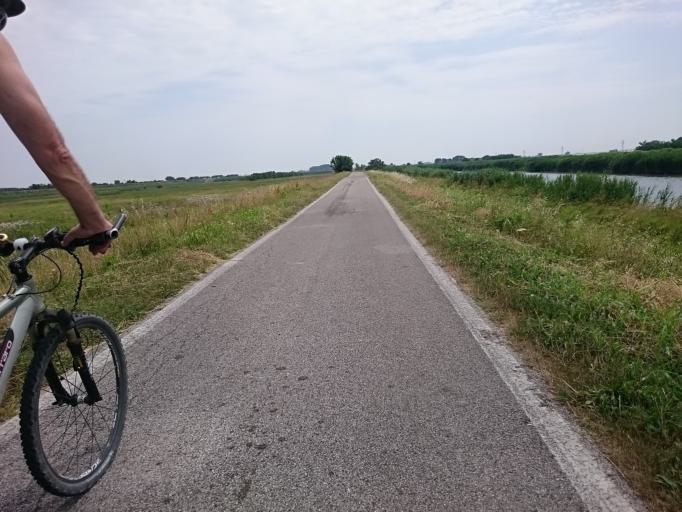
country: IT
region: Veneto
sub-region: Provincia di Venezia
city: Valli
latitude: 45.1894
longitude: 12.2184
